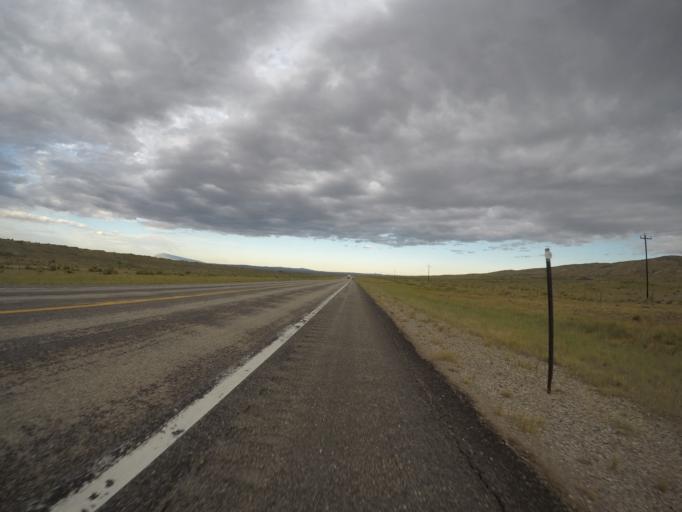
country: US
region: Wyoming
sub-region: Albany County
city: Laramie
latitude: 41.8650
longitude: -106.0897
